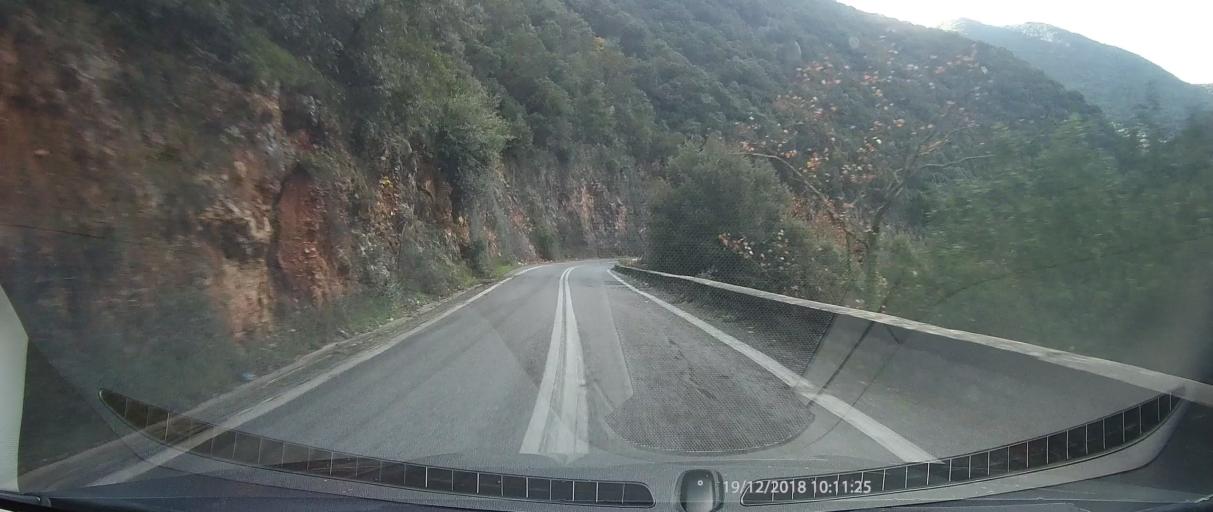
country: GR
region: Peloponnese
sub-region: Nomos Messinias
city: Kalamata
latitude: 37.0973
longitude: 22.1777
